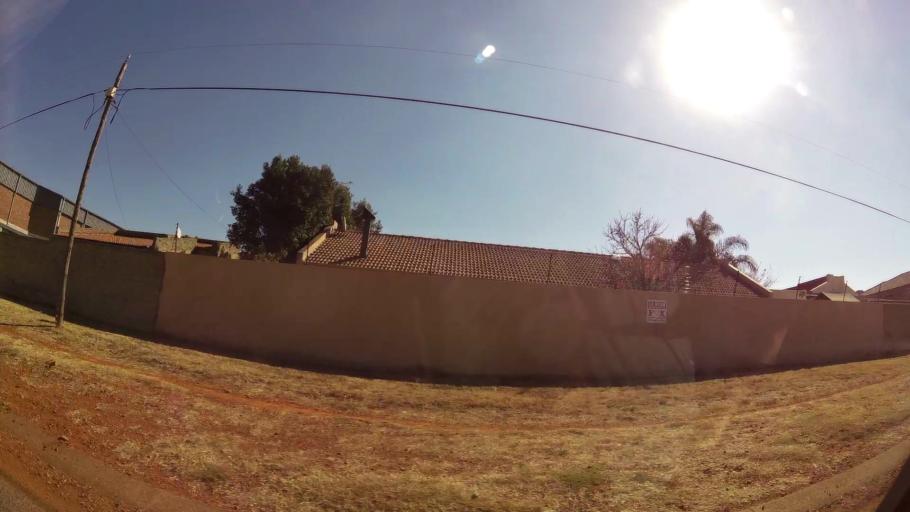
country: ZA
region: Gauteng
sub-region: Ekurhuleni Metropolitan Municipality
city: Germiston
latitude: -26.2987
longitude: 28.0976
